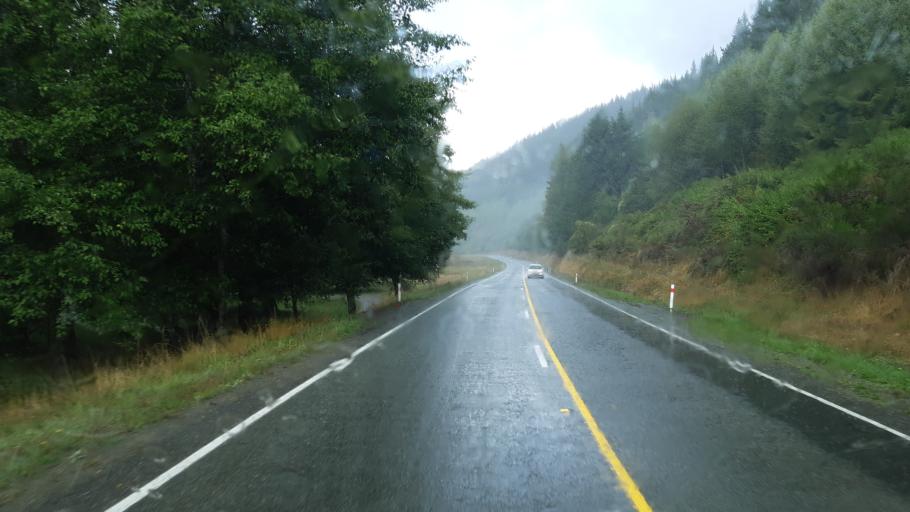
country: NZ
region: Tasman
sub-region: Tasman District
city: Wakefield
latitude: -41.4791
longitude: 172.8757
